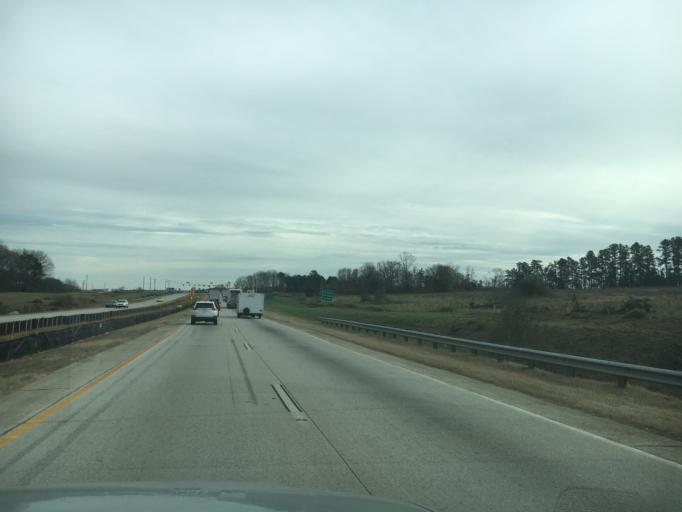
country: US
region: Georgia
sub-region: Barrow County
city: Winder
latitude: 33.9484
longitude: -83.7584
